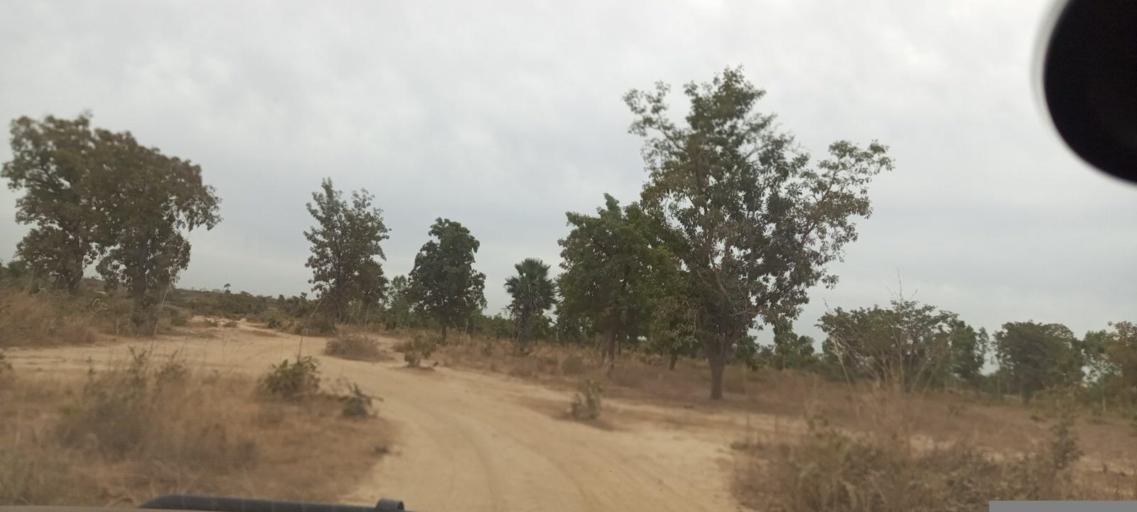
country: ML
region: Koulikoro
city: Kati
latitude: 12.7933
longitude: -8.2542
